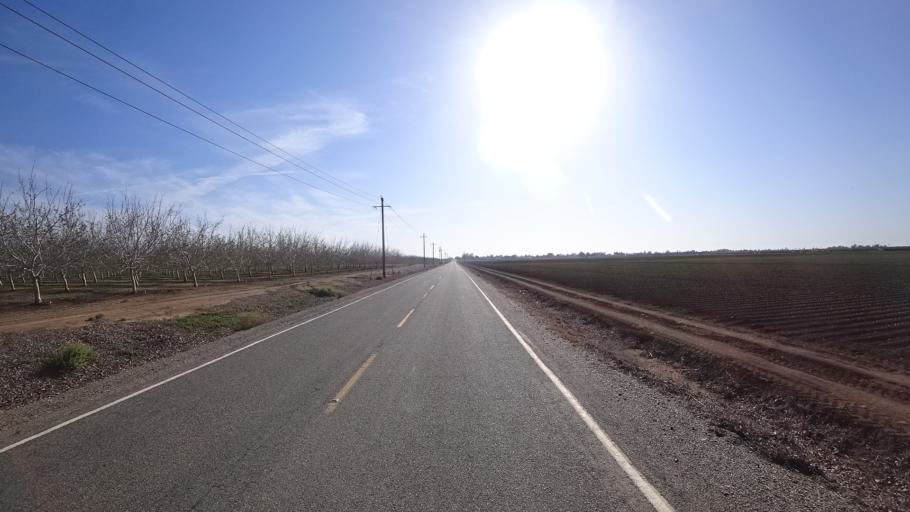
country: US
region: California
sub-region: Glenn County
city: Willows
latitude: 39.5388
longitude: -122.2279
